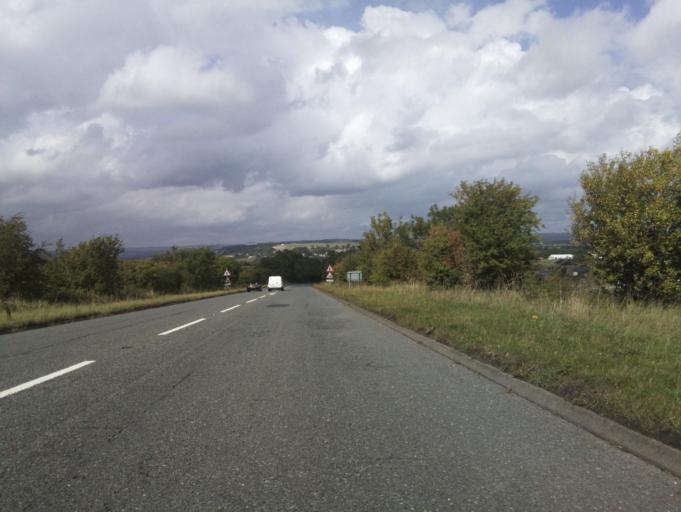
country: GB
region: England
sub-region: County Durham
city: High Etherley
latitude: 54.6589
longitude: -1.7715
